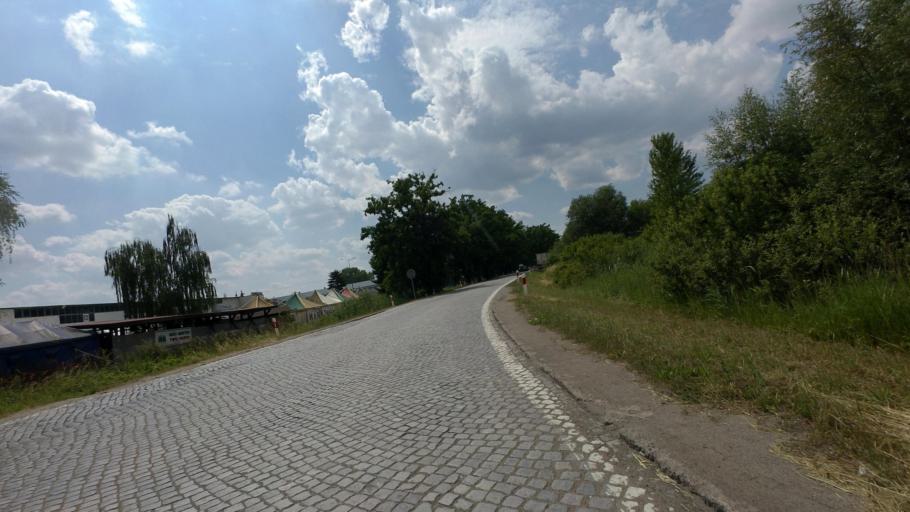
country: PL
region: West Pomeranian Voivodeship
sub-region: Powiat policki
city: Kolbaskowo
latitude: 53.3400
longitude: 14.4466
